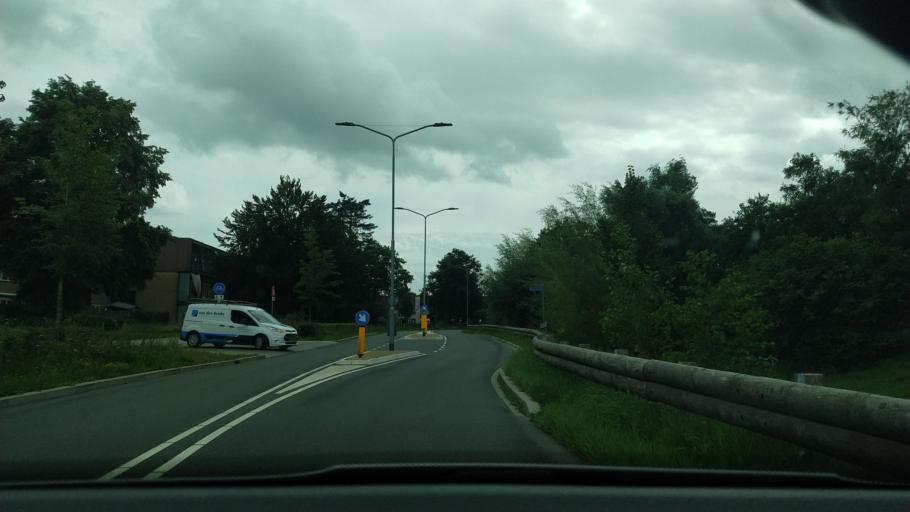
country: NL
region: Gelderland
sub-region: Gemeente Ermelo
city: Horst
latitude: 52.2929
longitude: 5.5972
